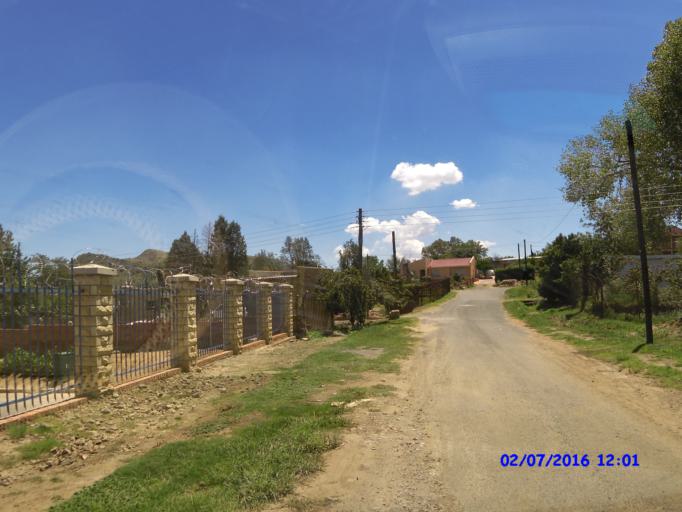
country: LS
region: Maseru
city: Maseru
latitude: -29.3030
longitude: 27.4596
